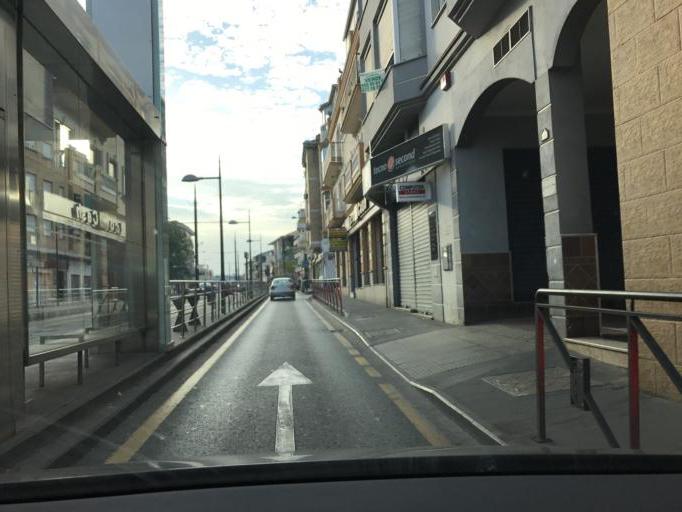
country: ES
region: Andalusia
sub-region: Provincia de Granada
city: Maracena
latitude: 37.2072
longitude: -3.6305
